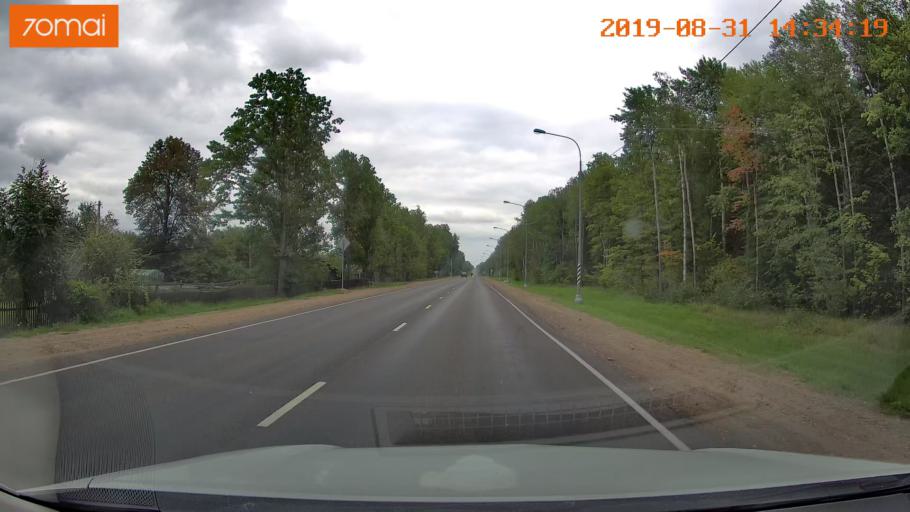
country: RU
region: Smolensk
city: Yekimovichi
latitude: 54.1568
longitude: 33.4354
